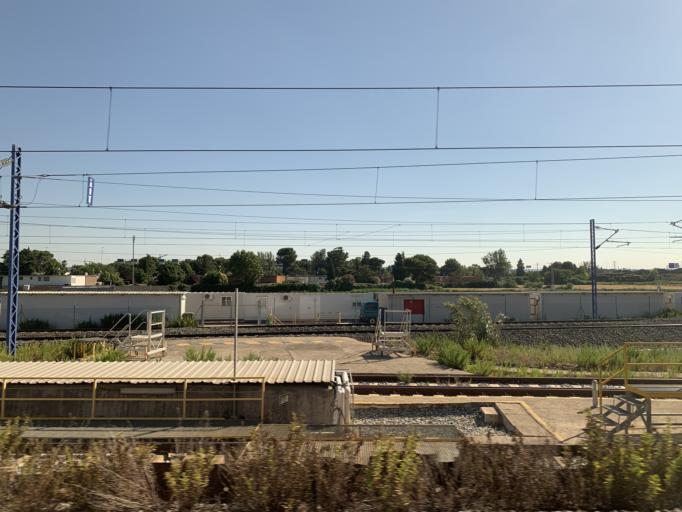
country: ES
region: Aragon
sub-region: Provincia de Zaragoza
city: Oliver-Valdefierro, Oliver, Valdefierro
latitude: 41.6690
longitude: -0.9296
